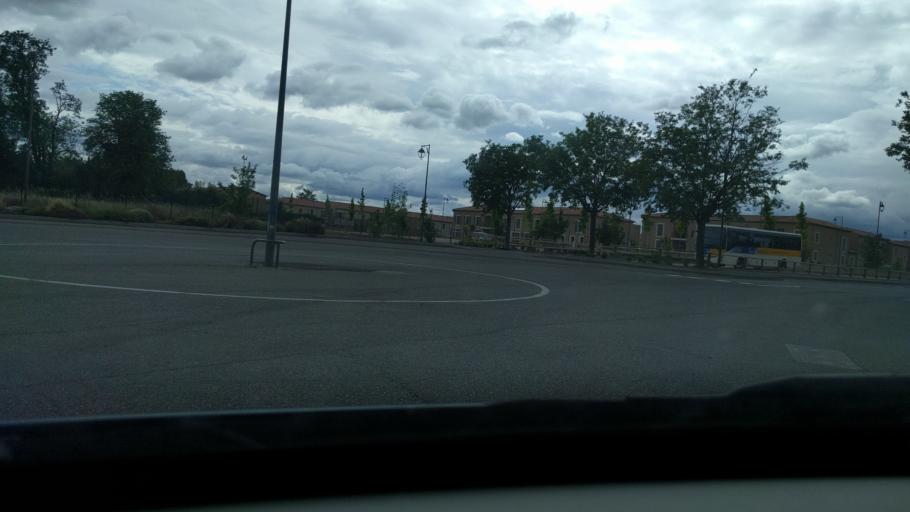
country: FR
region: Provence-Alpes-Cote d'Azur
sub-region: Departement du Vaucluse
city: Grambois
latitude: 43.7287
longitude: 5.5496
